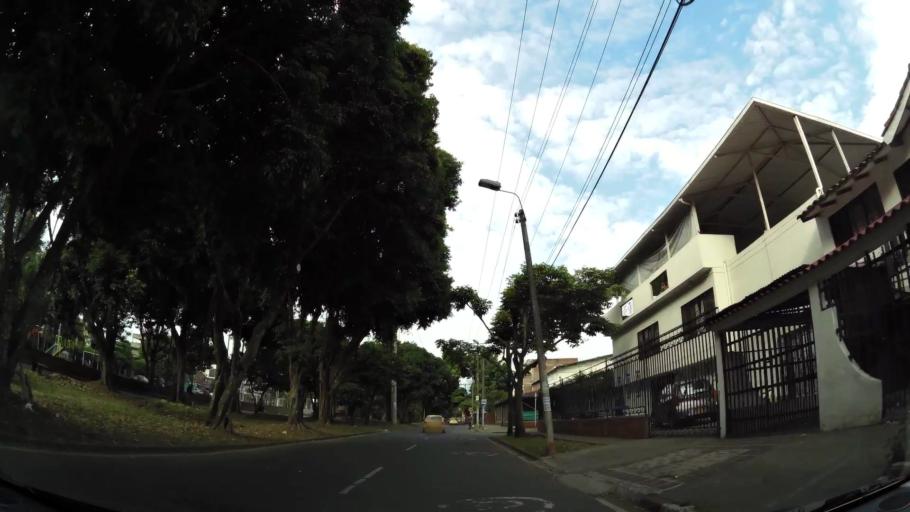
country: CO
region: Valle del Cauca
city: Cali
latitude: 3.4679
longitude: -76.4942
